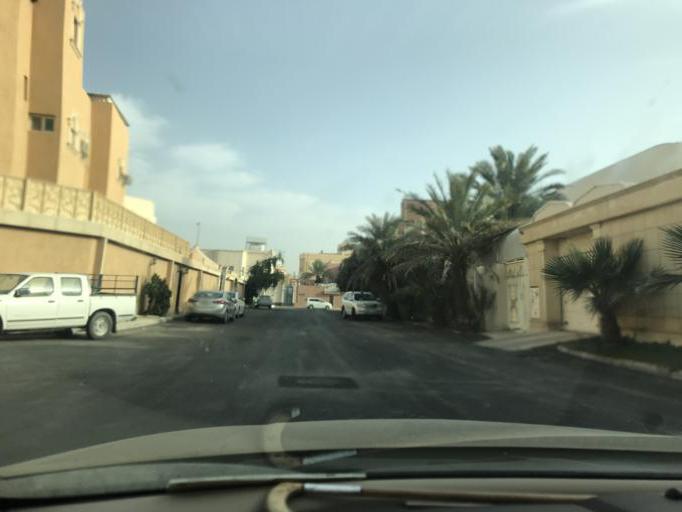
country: SA
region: Ar Riyad
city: Riyadh
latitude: 24.7394
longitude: 46.7504
